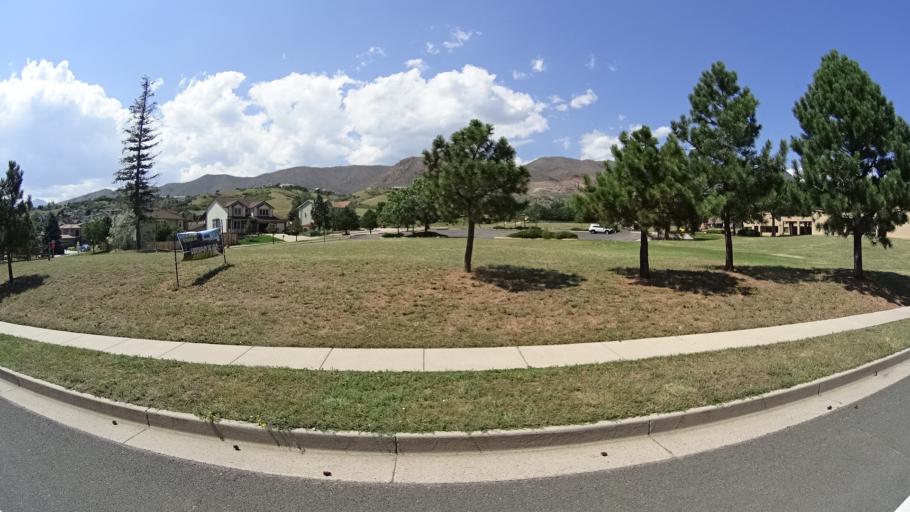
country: US
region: Colorado
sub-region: El Paso County
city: Air Force Academy
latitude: 38.9263
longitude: -104.8670
